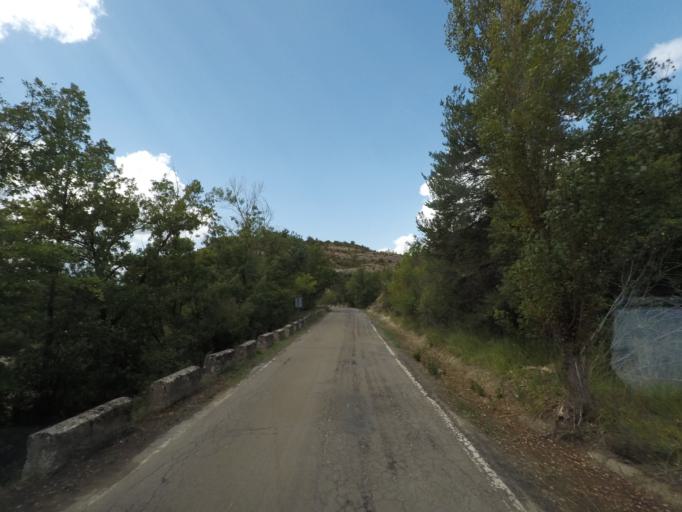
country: ES
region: Aragon
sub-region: Provincia de Huesca
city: Yebra de Basa
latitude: 42.3912
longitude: -0.2749
